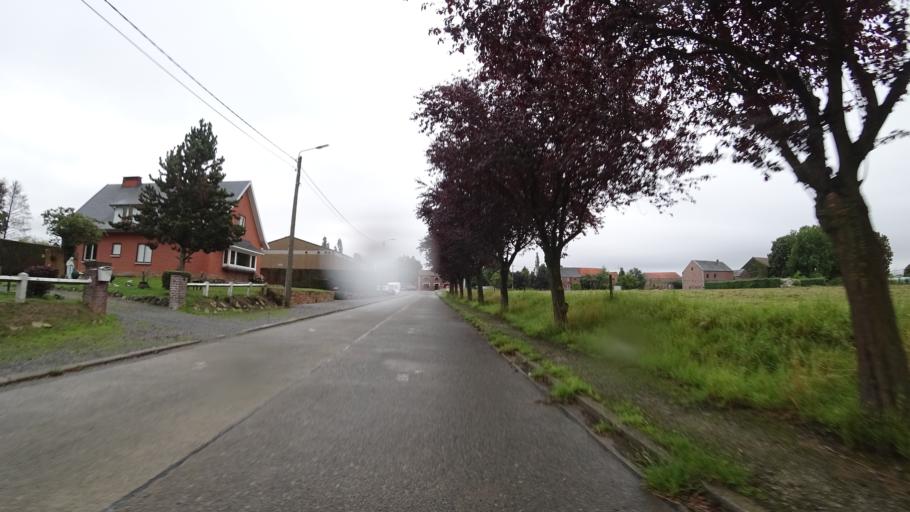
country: BE
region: Wallonia
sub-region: Province de Namur
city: Gembloux
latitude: 50.5359
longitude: 4.7807
